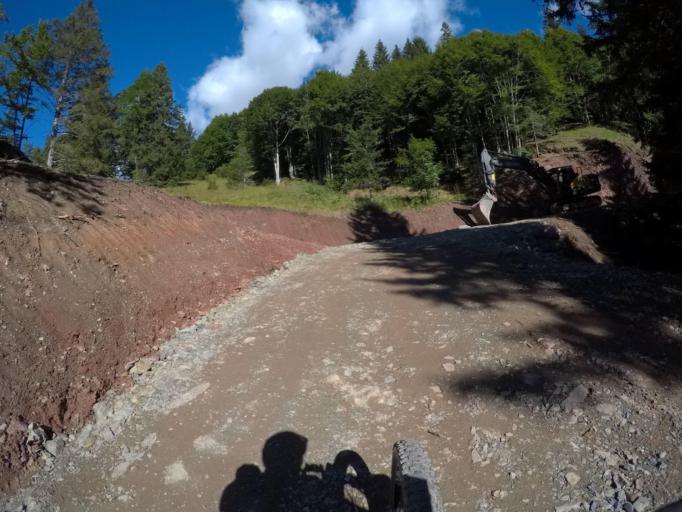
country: IT
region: Friuli Venezia Giulia
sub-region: Provincia di Udine
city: Ligosullo
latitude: 46.5508
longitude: 13.0926
